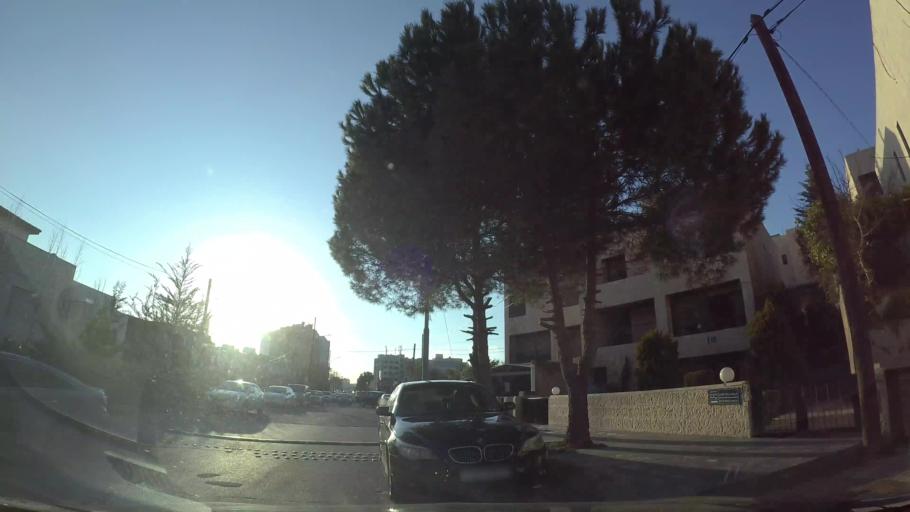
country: JO
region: Amman
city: Al Jubayhah
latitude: 31.9772
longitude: 35.8680
